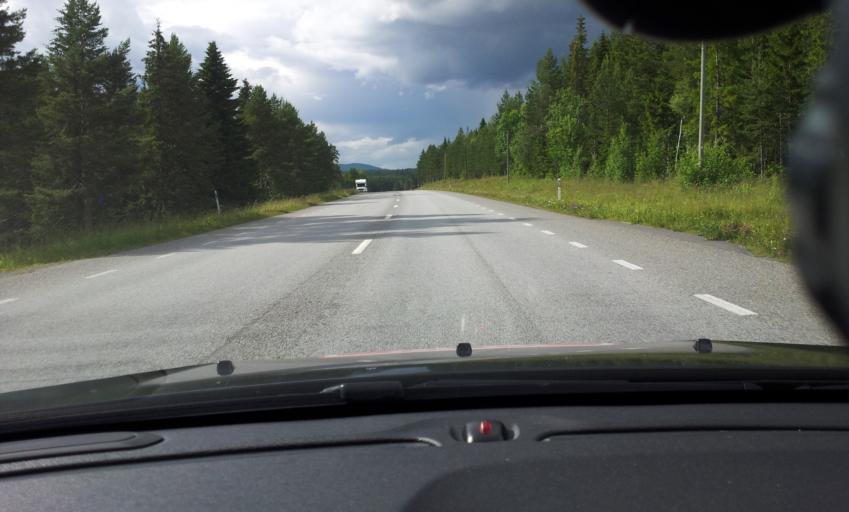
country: SE
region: Jaemtland
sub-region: Are Kommun
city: Jarpen
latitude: 63.3272
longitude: 13.5349
